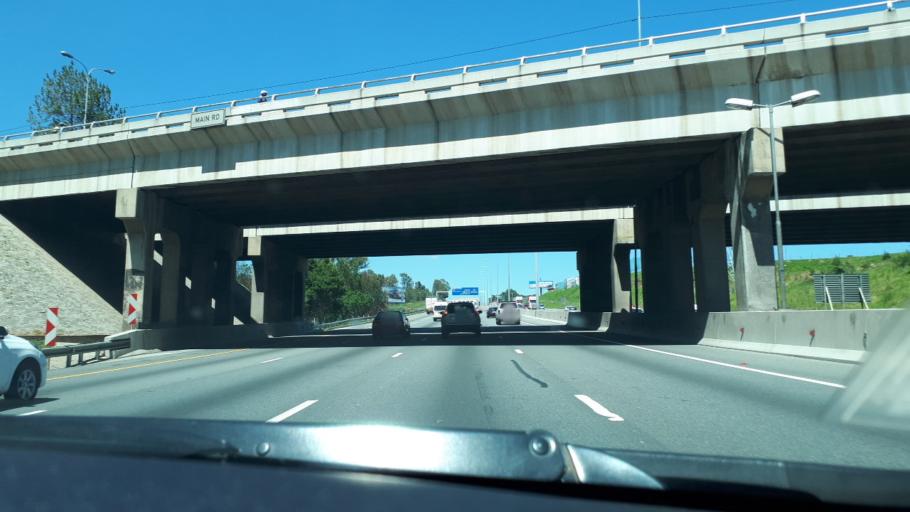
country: ZA
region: Gauteng
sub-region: City of Johannesburg Metropolitan Municipality
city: Diepsloot
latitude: -26.0350
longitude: 28.0268
